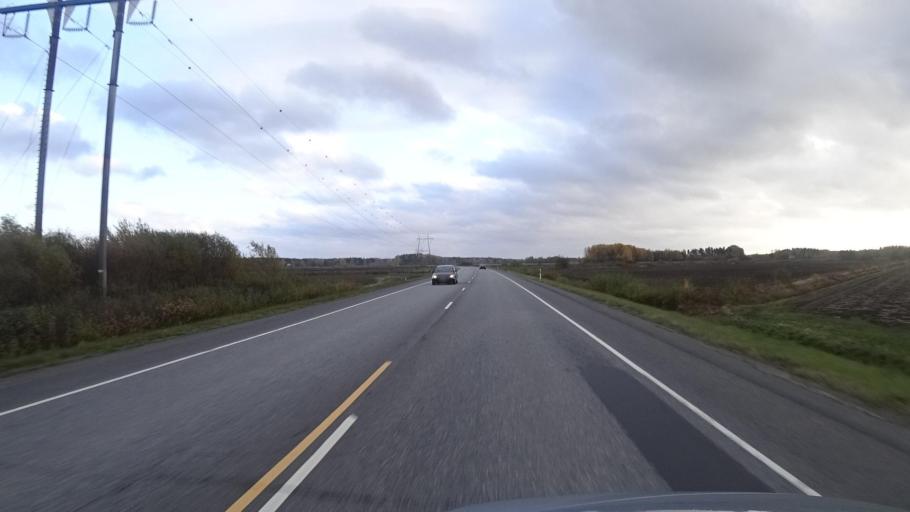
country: FI
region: Satakunta
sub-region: Rauma
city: Saekylae
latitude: 61.0350
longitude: 22.3897
